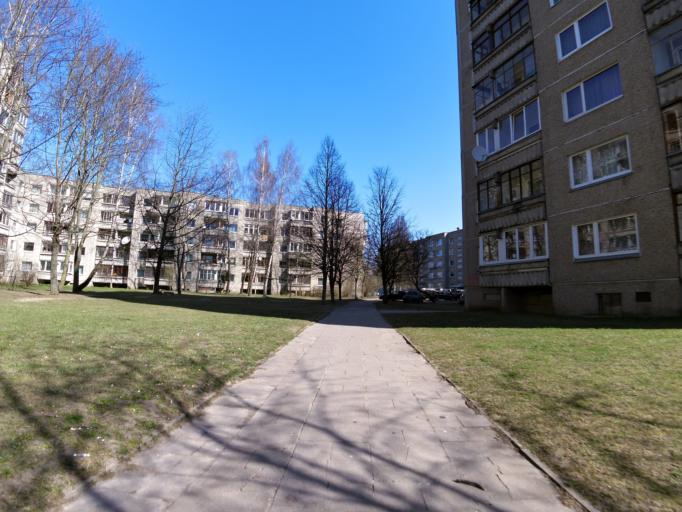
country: LT
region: Vilnius County
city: Justiniskes
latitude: 54.7199
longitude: 25.2209
